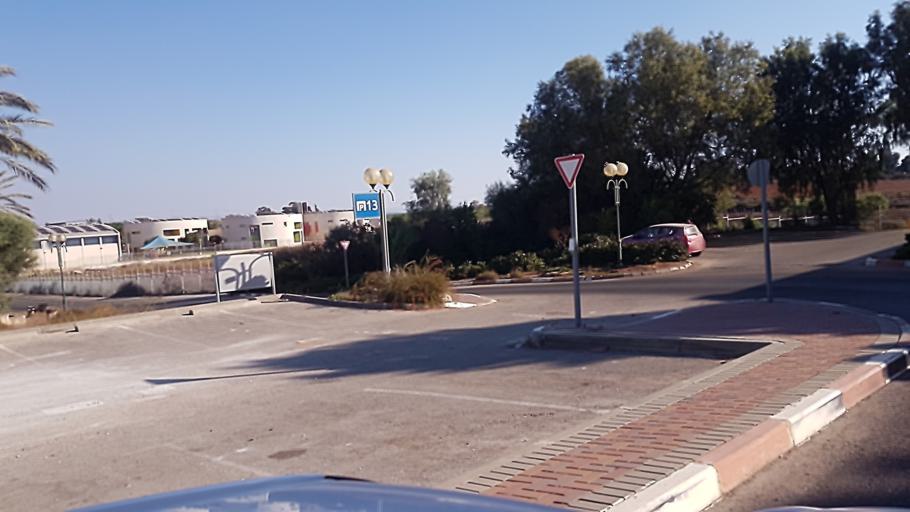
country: IL
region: Central District
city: Kfar Saba
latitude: 32.2010
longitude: 34.9191
